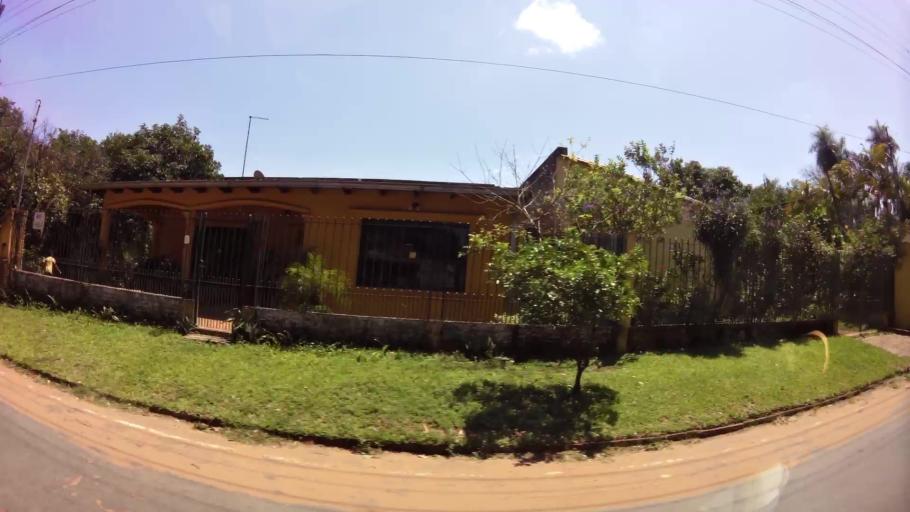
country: PY
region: Central
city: San Antonio
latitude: -25.4290
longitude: -57.5366
